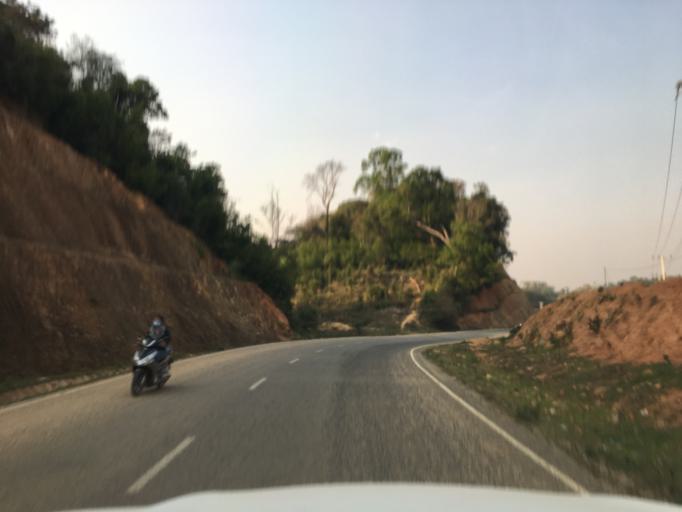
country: LA
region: Houaphan
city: Xam Nua
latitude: 20.5975
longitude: 104.0683
